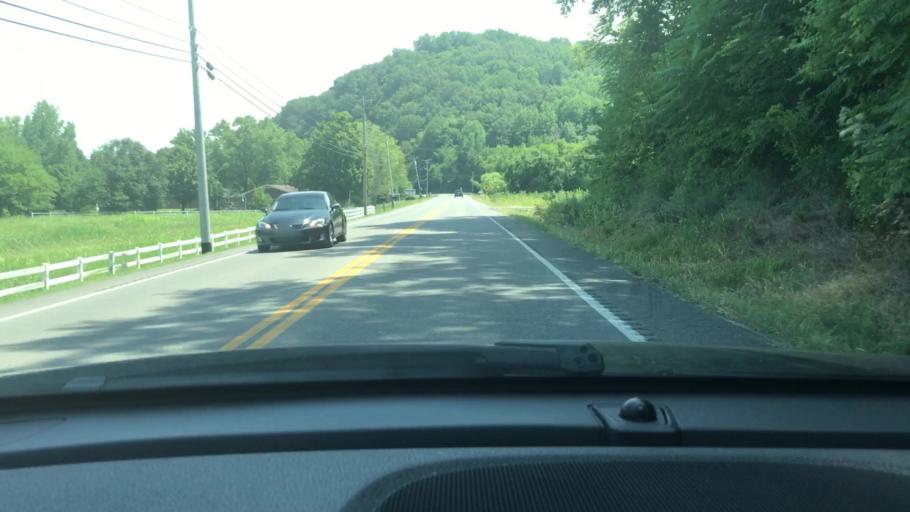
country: US
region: Tennessee
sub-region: Sumner County
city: Shackle Island
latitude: 36.3968
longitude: -86.6292
